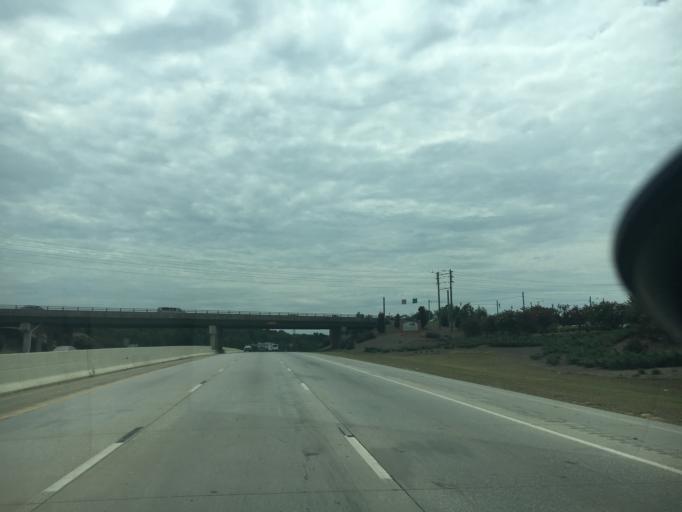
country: US
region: South Carolina
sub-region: Greenville County
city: Mauldin
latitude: 34.8069
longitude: -82.2838
